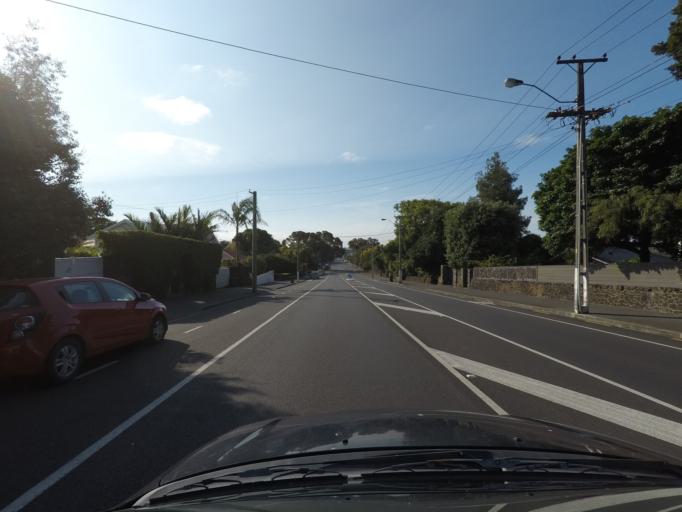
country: NZ
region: Auckland
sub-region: Auckland
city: Rosebank
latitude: -36.8861
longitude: 174.7185
